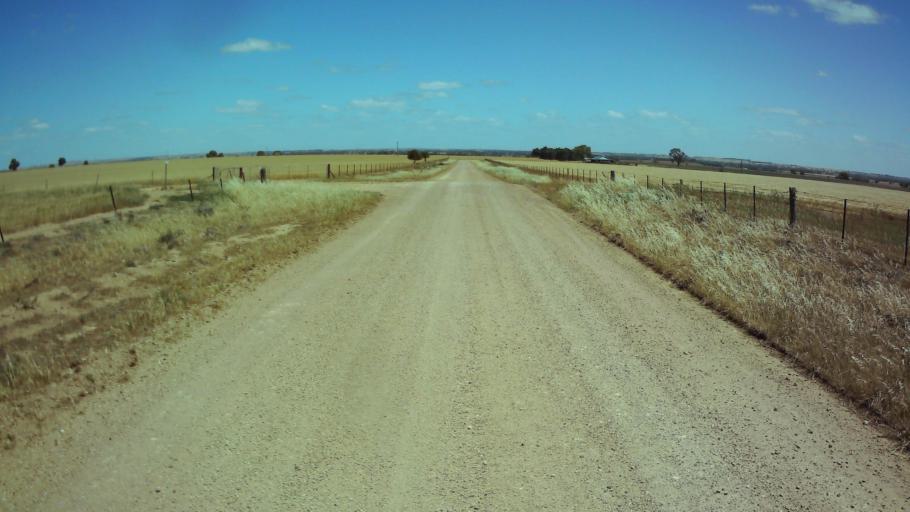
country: AU
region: New South Wales
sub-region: Weddin
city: Grenfell
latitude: -33.9676
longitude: 148.3304
